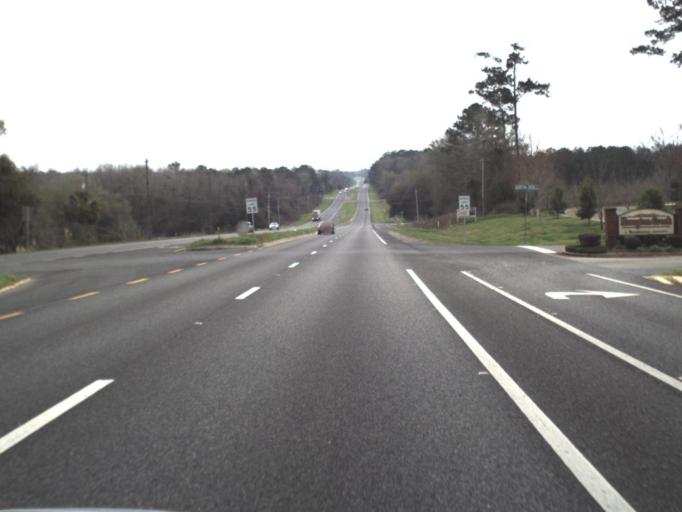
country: US
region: Florida
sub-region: Leon County
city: Tallahassee
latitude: 30.4262
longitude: -84.1836
